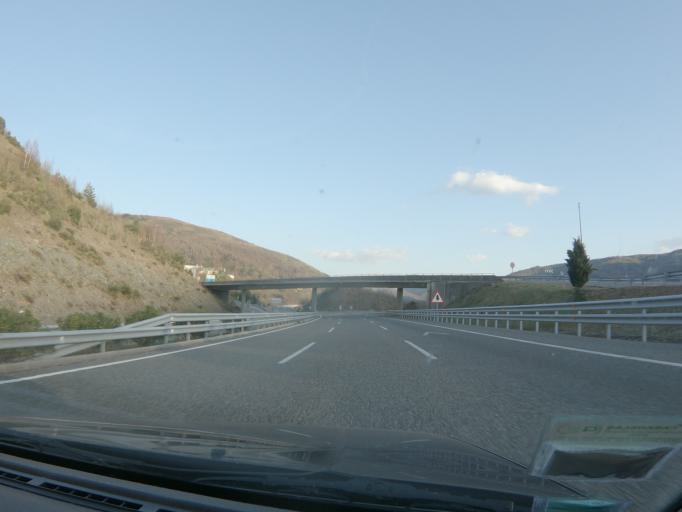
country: ES
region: Galicia
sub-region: Provincia de Lugo
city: San Roman
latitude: 42.7655
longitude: -7.0852
